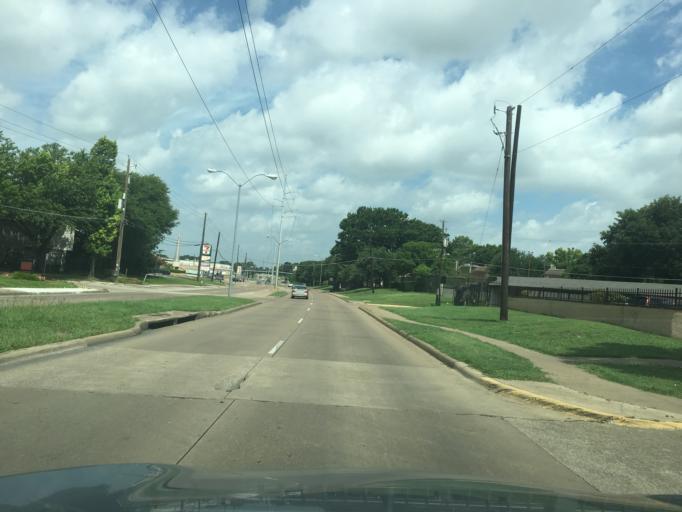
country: US
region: Texas
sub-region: Dallas County
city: Richardson
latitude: 32.9213
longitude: -96.7146
